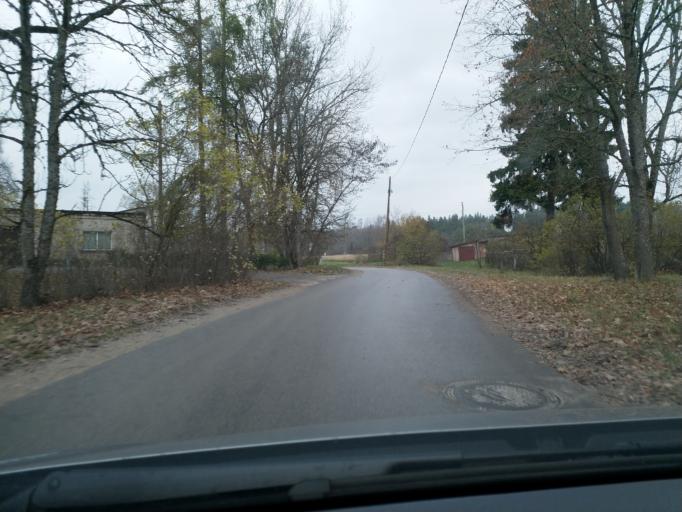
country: LV
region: Kuldigas Rajons
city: Kuldiga
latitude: 56.9816
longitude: 21.9742
